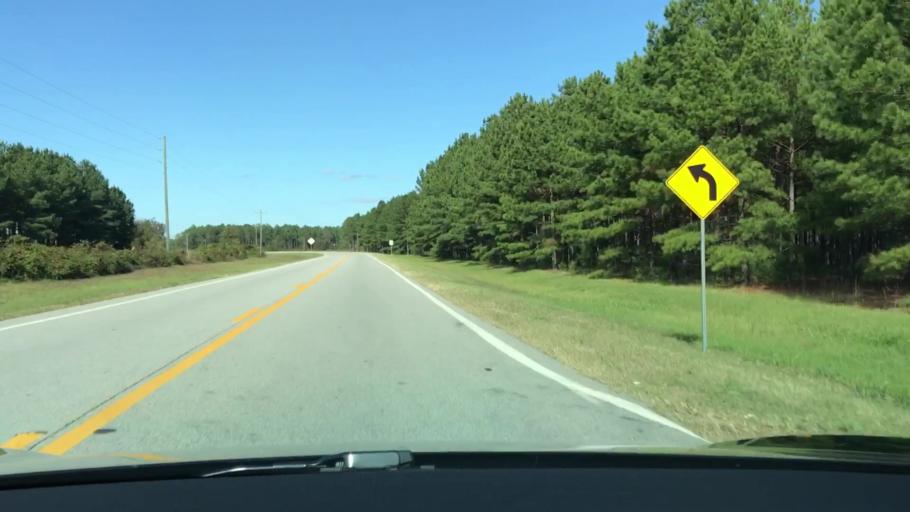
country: US
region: Georgia
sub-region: Glascock County
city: Gibson
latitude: 33.3032
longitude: -82.5223
